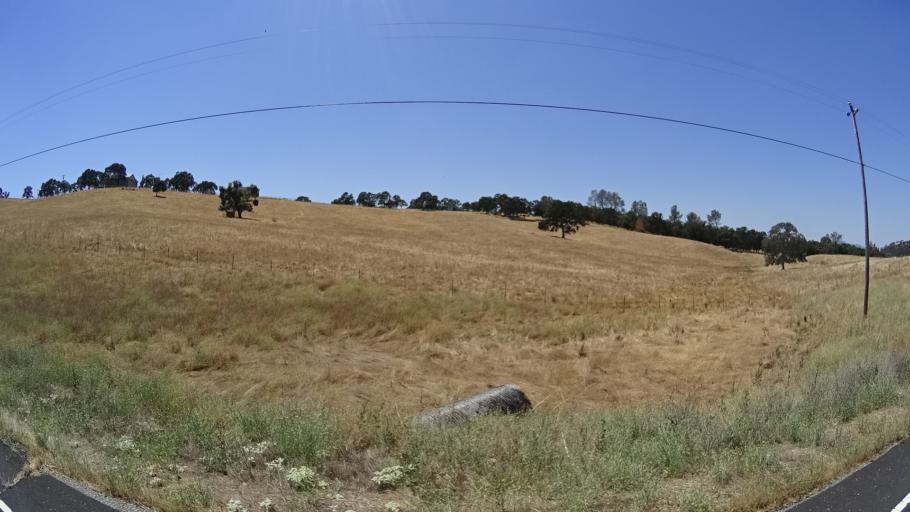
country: US
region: California
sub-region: Calaveras County
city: Angels Camp
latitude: 38.0316
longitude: -120.5273
